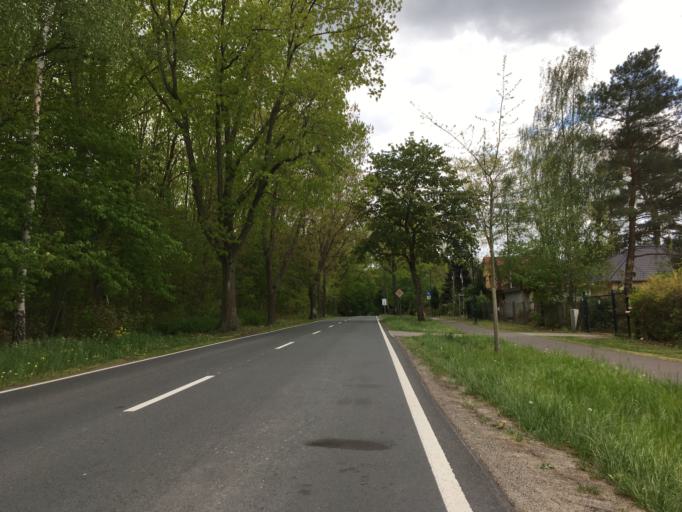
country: DE
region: Brandenburg
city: Bernau bei Berlin
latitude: 52.6310
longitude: 13.6116
